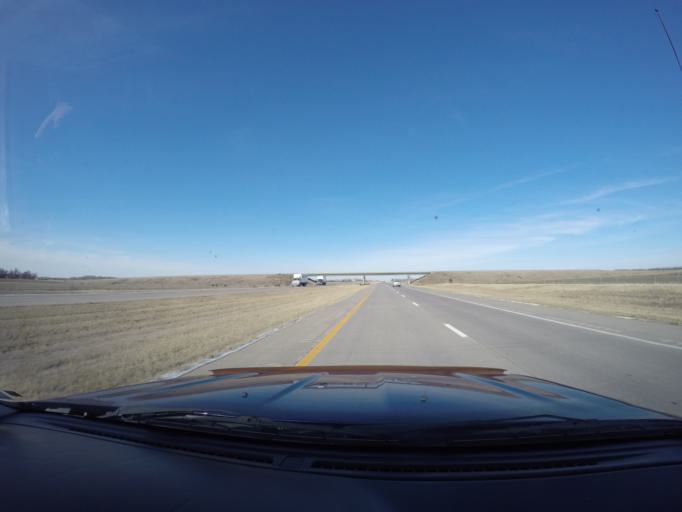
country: US
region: Kansas
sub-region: Sedgwick County
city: Valley Center
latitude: 37.8812
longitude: -97.3264
